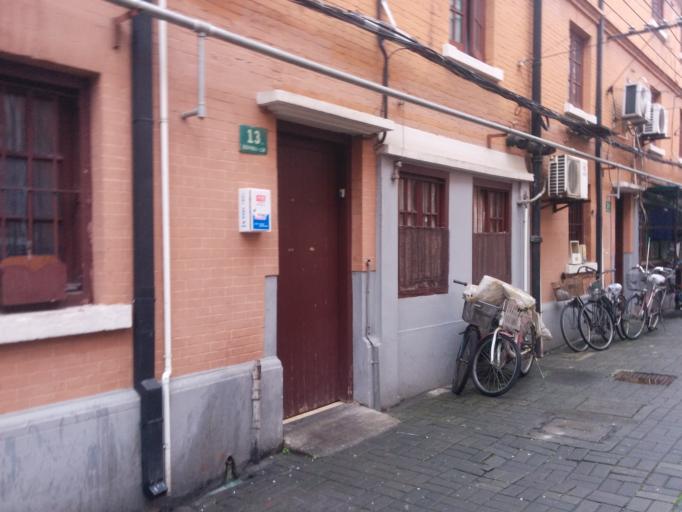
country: CN
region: Shanghai Shi
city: Shanghai
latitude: 31.2247
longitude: 121.4482
